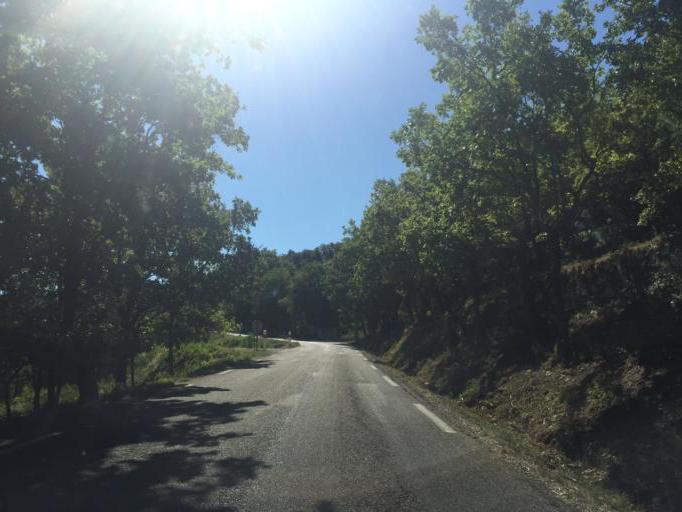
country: FR
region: Provence-Alpes-Cote d'Azur
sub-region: Departement du Vaucluse
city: Venasque
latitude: 43.9978
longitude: 5.1477
